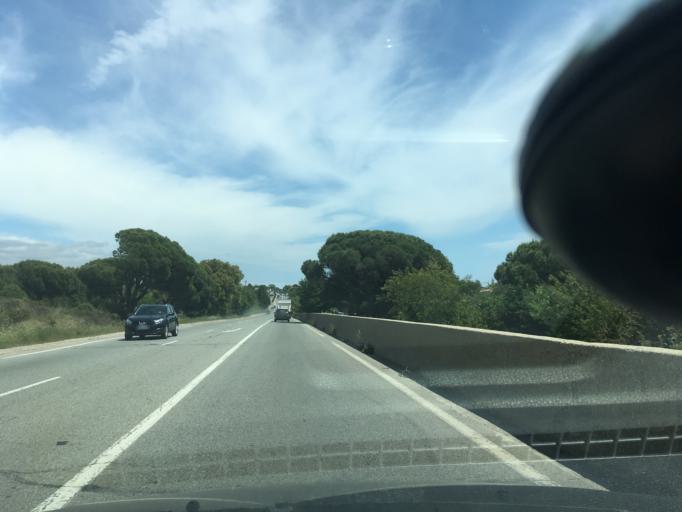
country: FR
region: Provence-Alpes-Cote d'Azur
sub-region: Departement du Var
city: Puget-sur-Argens
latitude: 43.4586
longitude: 6.6724
